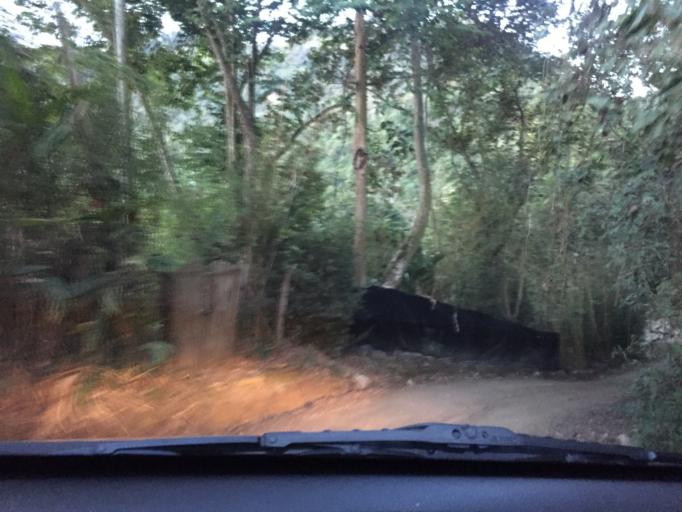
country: CO
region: Cundinamarca
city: Zipacon
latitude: 4.7088
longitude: -74.4080
